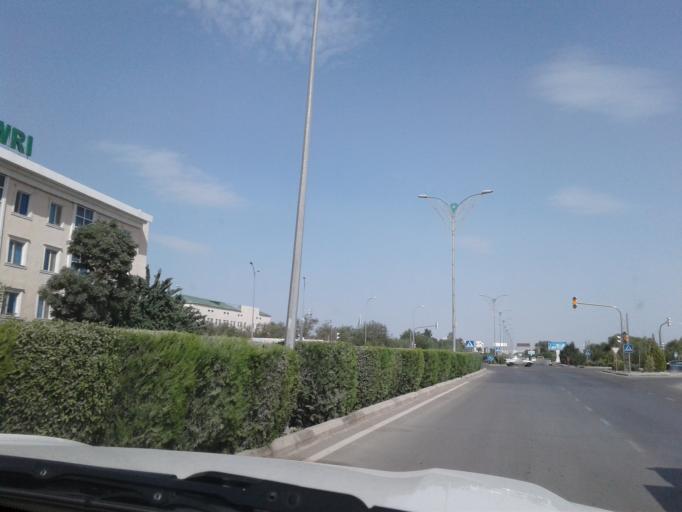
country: TM
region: Dasoguz
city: Dasoguz
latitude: 41.8302
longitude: 59.9440
